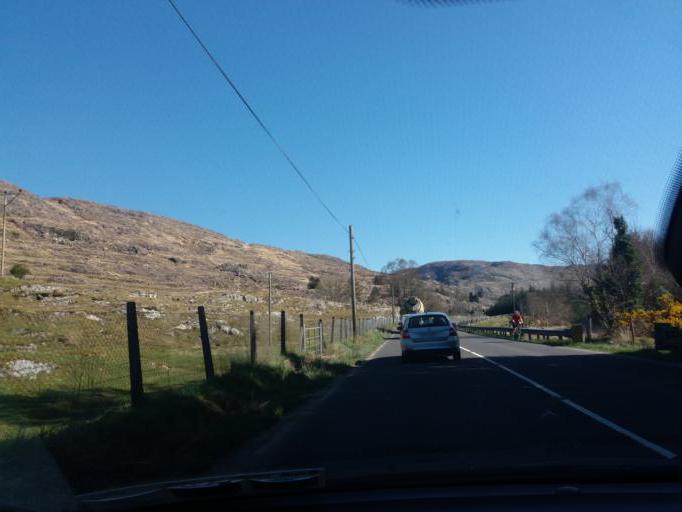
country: IE
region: Munster
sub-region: Ciarrai
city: Cill Airne
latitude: 51.9704
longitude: -9.3480
